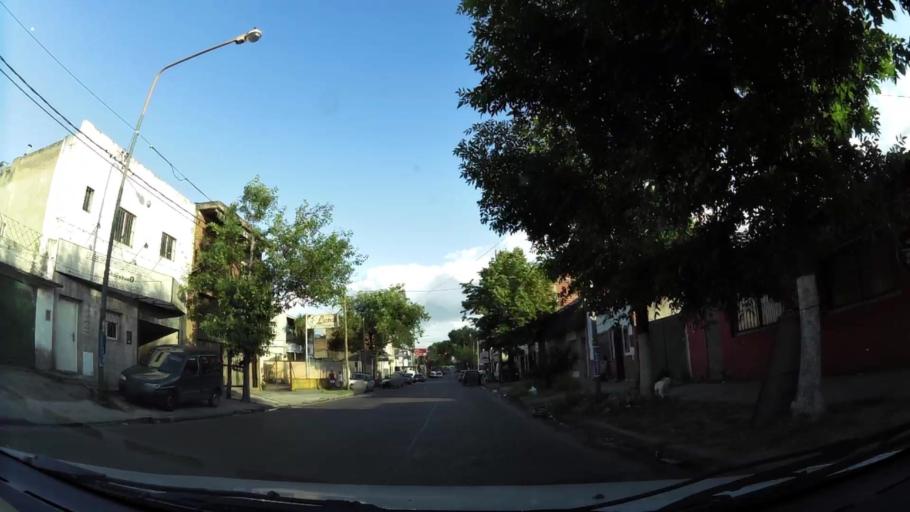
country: AR
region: Buenos Aires
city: Caseros
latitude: -34.5564
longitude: -58.5721
